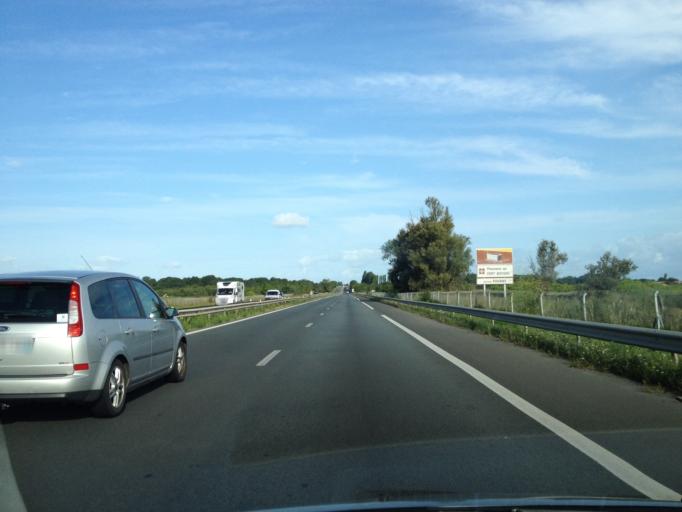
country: FR
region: Poitou-Charentes
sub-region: Departement de la Charente-Maritime
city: Saint-Laurent-de-la-Pree
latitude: 45.9832
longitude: -1.0198
